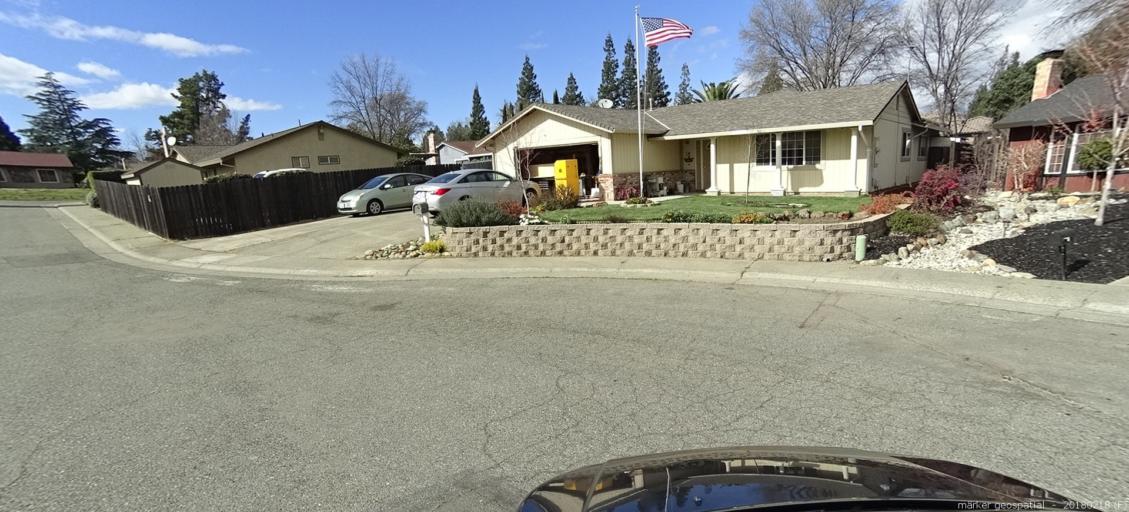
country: US
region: California
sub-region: Sacramento County
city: Orangevale
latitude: 38.6733
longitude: -121.2128
